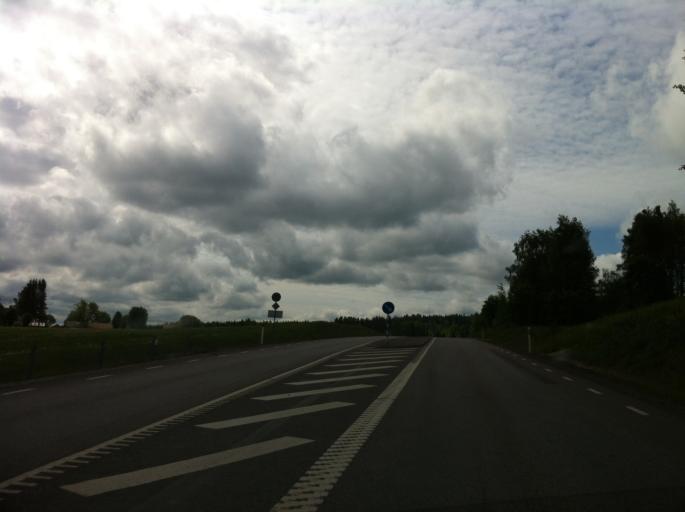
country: SE
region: Vaermland
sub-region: Sunne Kommun
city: Sunne
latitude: 59.7914
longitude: 13.0975
